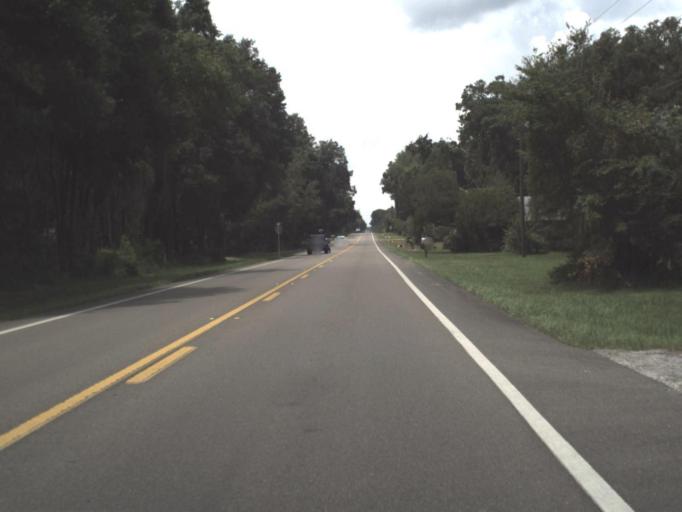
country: US
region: Florida
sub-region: Levy County
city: Williston
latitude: 29.4423
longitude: -82.4666
